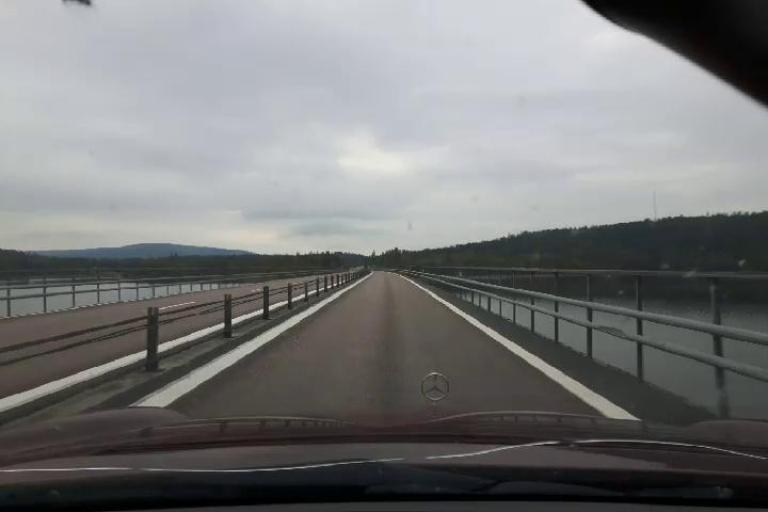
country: SE
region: Vaesternorrland
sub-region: Kramfors Kommun
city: Nordingra
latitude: 62.9042
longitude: 18.0932
